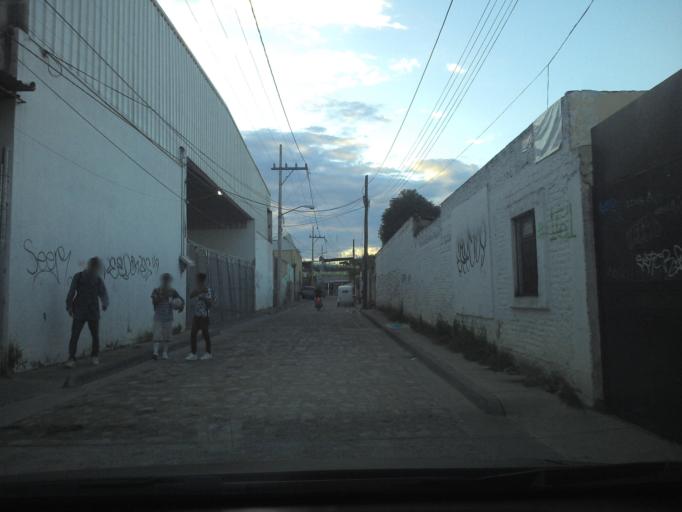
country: MX
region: Jalisco
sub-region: Tlajomulco de Zuniga
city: Palomar
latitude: 20.6192
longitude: -103.4517
